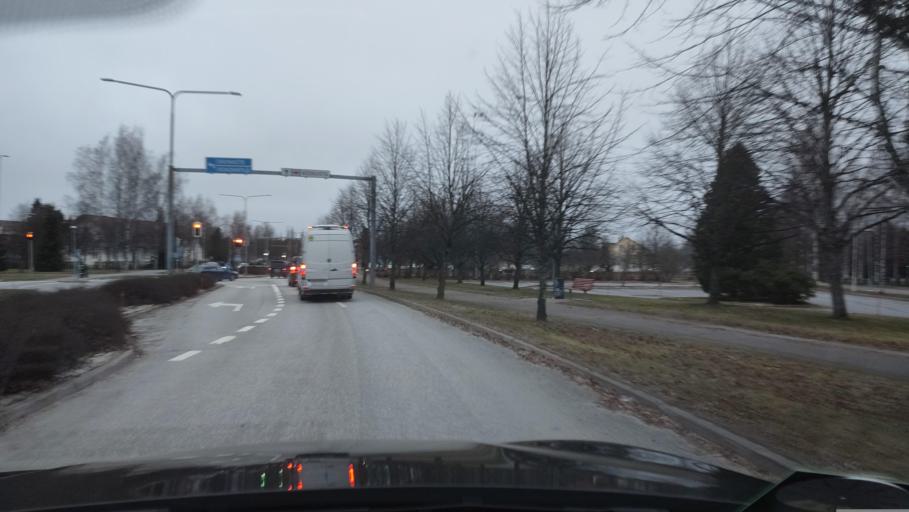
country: FI
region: Southern Ostrobothnia
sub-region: Suupohja
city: Kauhajoki
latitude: 62.4202
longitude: 22.1765
